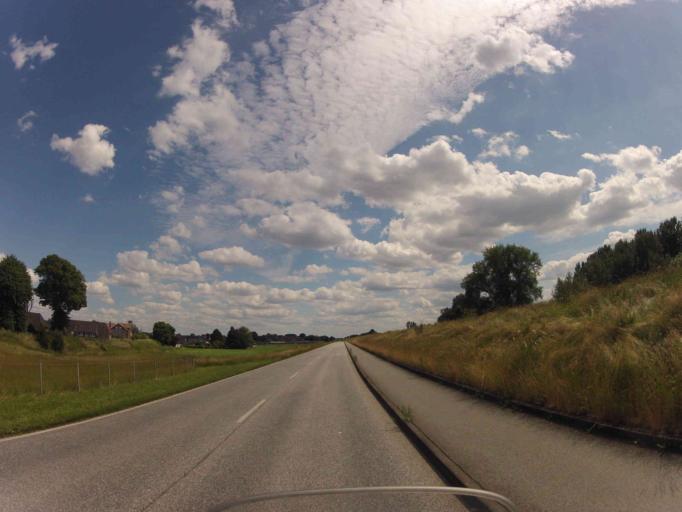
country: DE
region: Lower Saxony
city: Stelle
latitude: 53.4106
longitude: 10.1533
